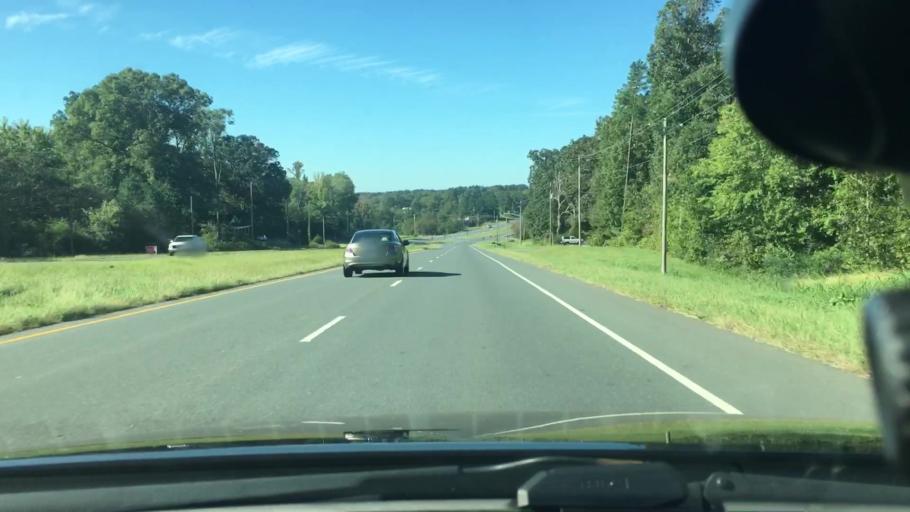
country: US
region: North Carolina
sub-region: Stanly County
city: Albemarle
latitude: 35.3112
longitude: -80.2636
